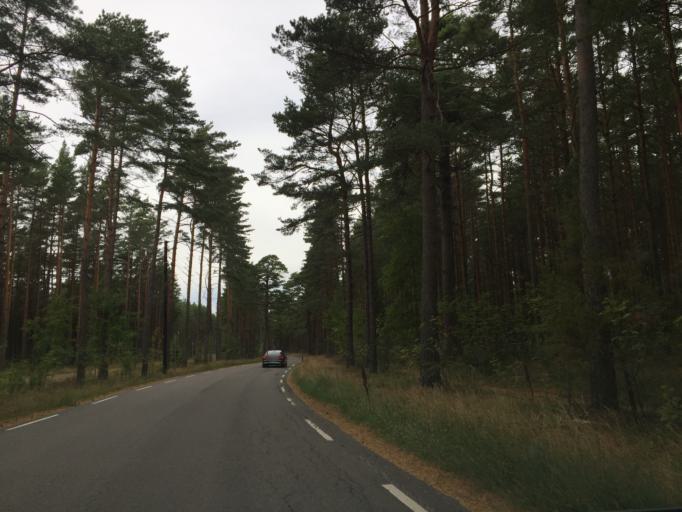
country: NO
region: Ostfold
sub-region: Hvaler
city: Skjaerhalden
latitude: 59.0289
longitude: 11.0297
